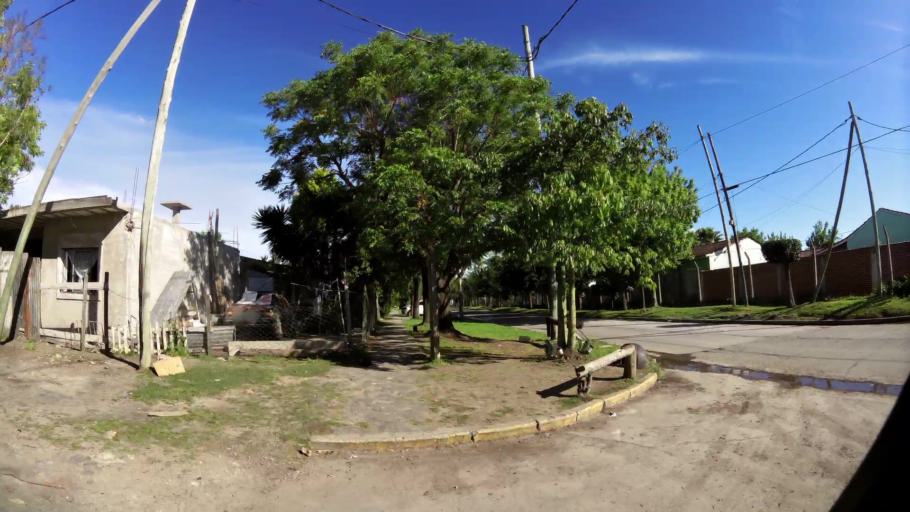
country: AR
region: Buenos Aires
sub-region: Partido de Almirante Brown
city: Adrogue
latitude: -34.8283
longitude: -58.3511
